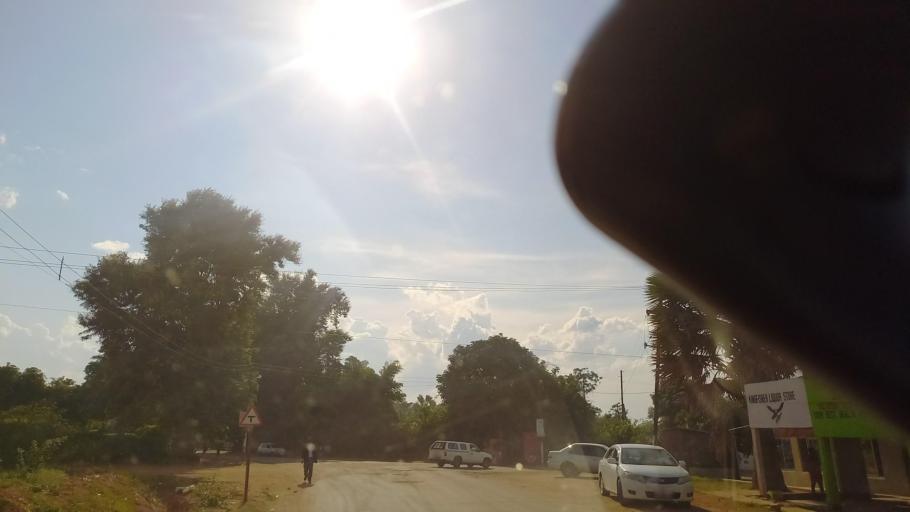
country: ZM
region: Southern
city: Mazabuka
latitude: -15.8613
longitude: 27.7611
